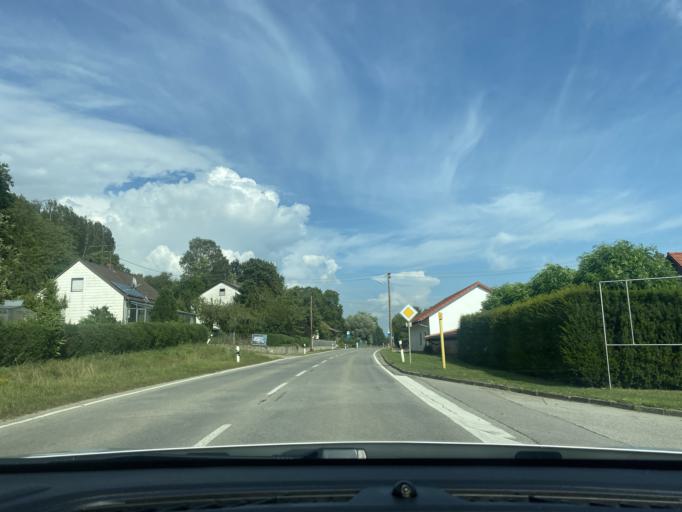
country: DE
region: Bavaria
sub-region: Upper Bavaria
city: Haag an der Amper
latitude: 48.4577
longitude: 11.8108
